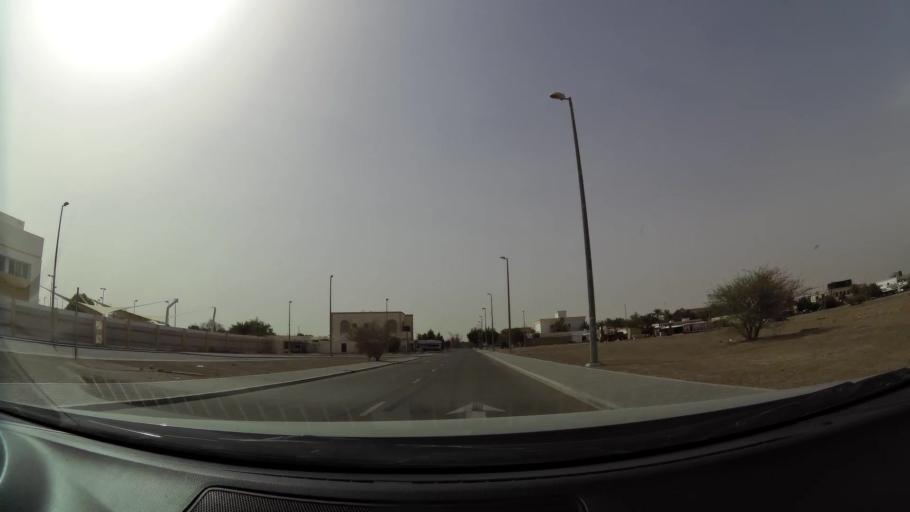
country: AE
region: Abu Dhabi
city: Al Ain
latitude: 24.1827
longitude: 55.6128
